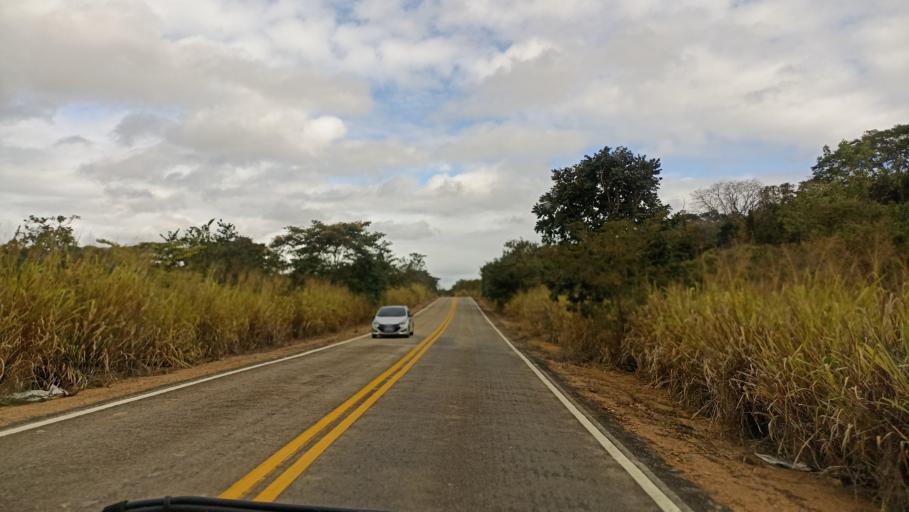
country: BR
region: Minas Gerais
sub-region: Joaima
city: Joaima
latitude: -16.6914
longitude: -40.9590
